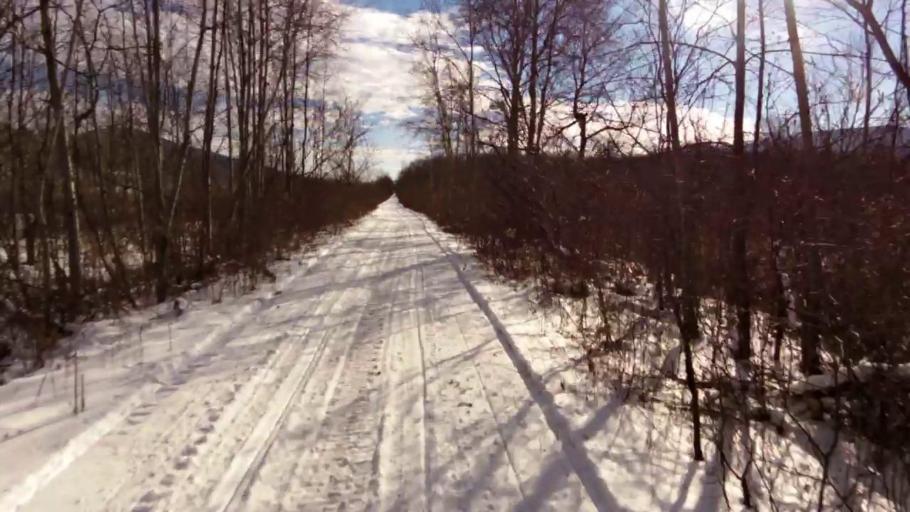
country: US
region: Pennsylvania
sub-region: McKean County
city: Foster Brook
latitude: 42.0336
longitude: -78.6328
